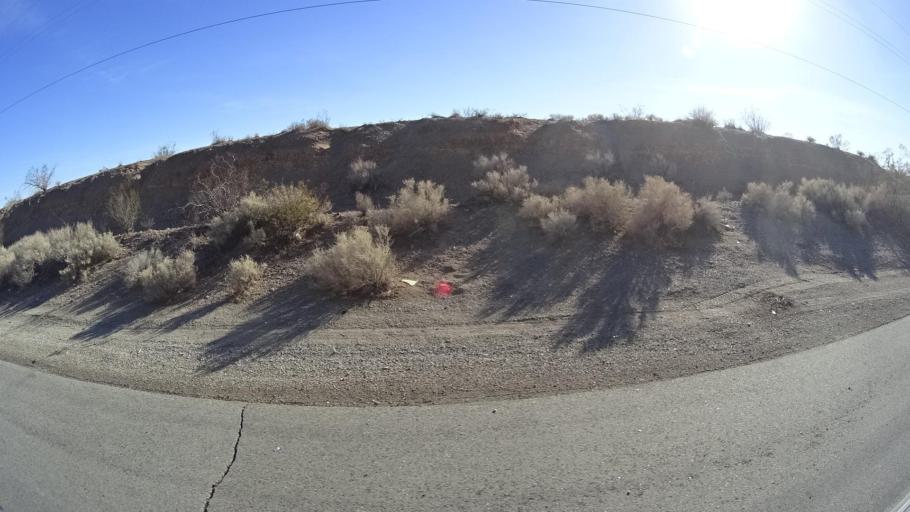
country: US
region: California
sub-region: Kern County
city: Ridgecrest
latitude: 35.6225
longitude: -117.7188
